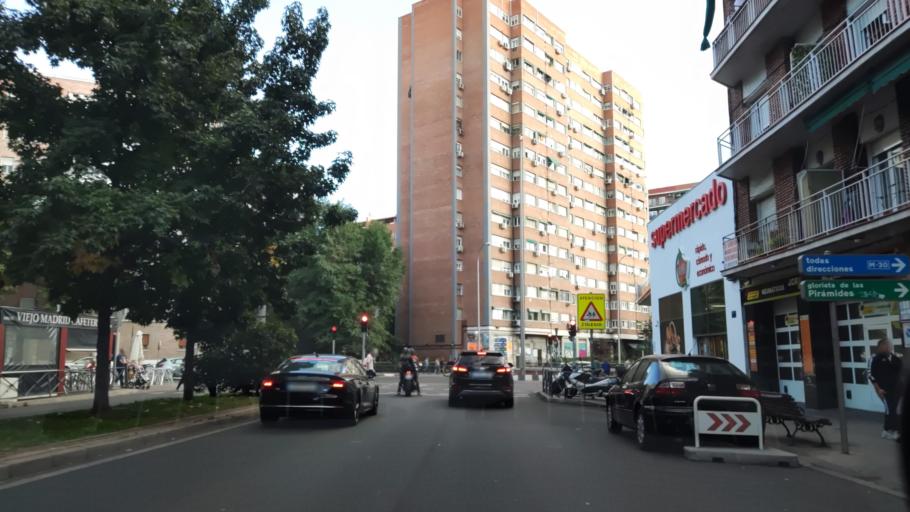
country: ES
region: Madrid
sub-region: Provincia de Madrid
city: Arganzuela
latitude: 40.3982
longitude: -3.7026
